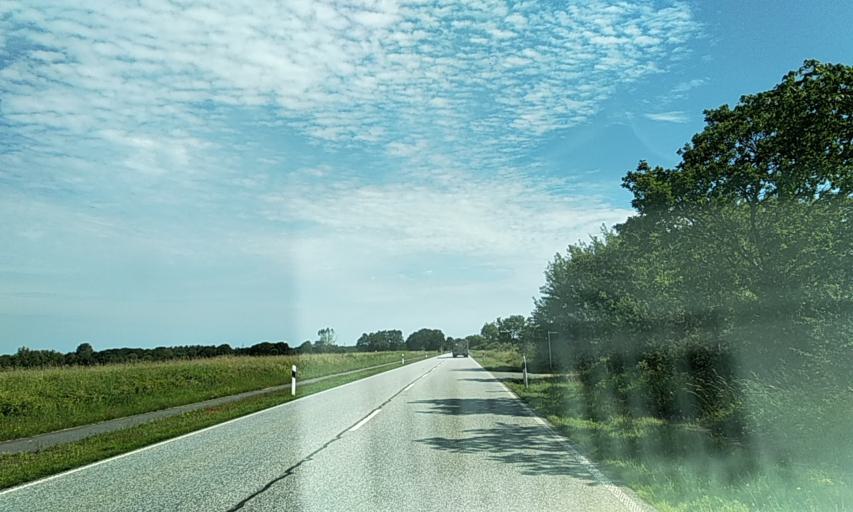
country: DE
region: Schleswig-Holstein
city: Jagel
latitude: 54.4656
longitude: 9.5411
